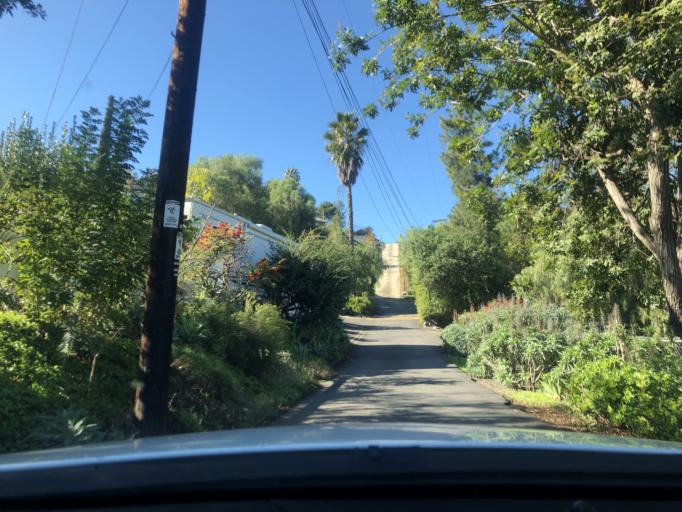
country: US
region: California
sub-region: San Diego County
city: El Cajon
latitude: 32.7851
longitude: -116.9429
